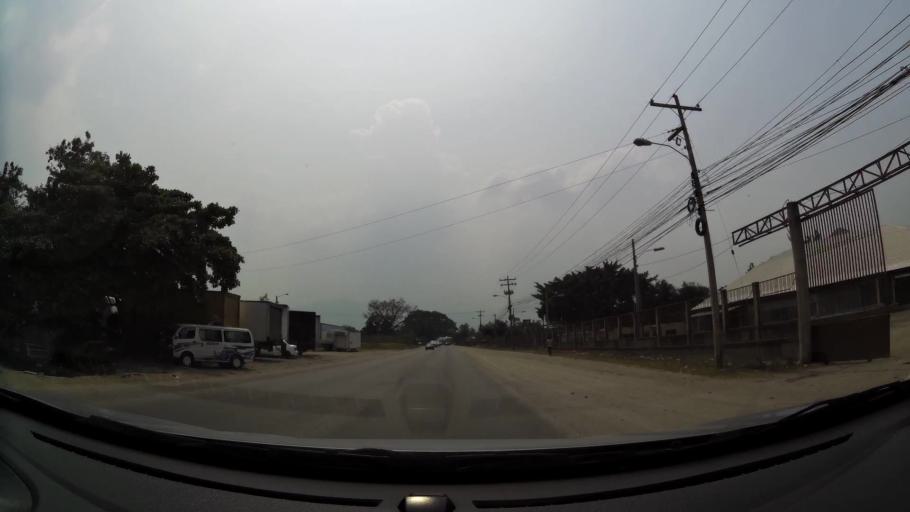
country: HN
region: Cortes
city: San Pedro Sula
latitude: 15.4704
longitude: -87.9938
